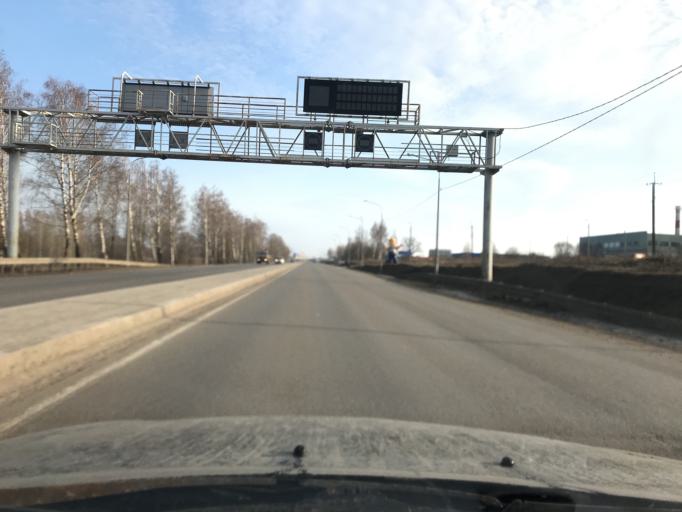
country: RU
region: Kaluga
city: Kaluga
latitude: 54.4889
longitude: 36.2294
